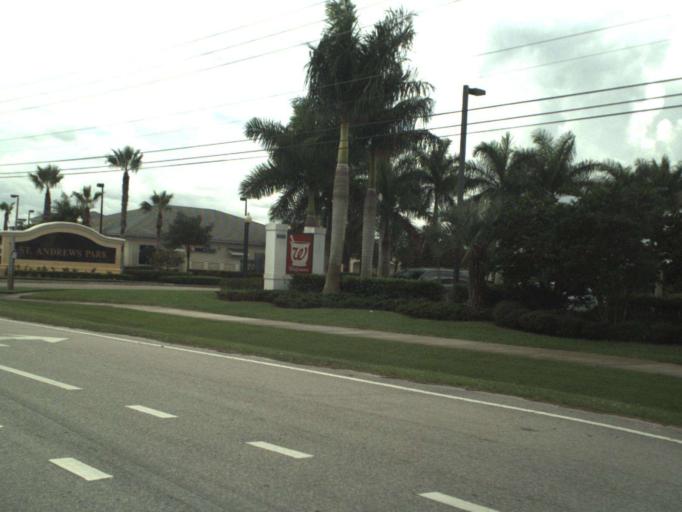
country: US
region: Florida
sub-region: Saint Lucie County
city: White City
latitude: 27.3572
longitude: -80.3581
